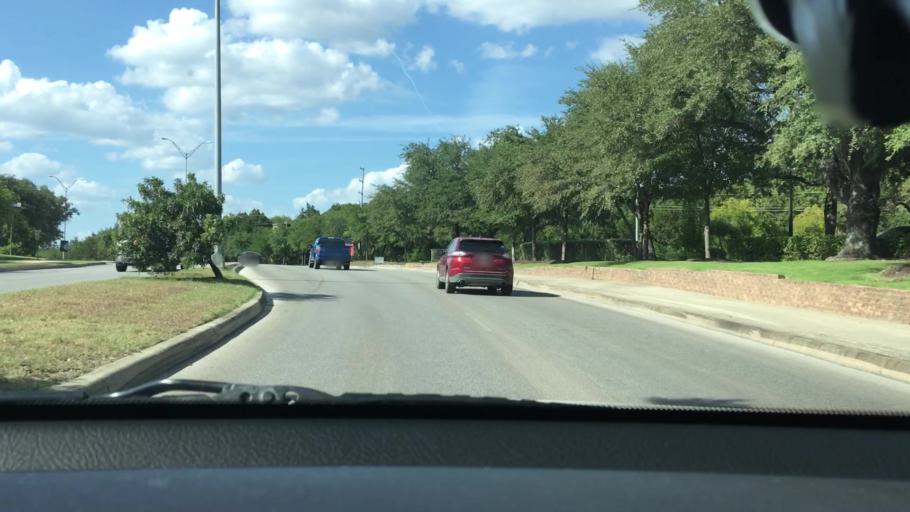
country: US
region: Texas
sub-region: Bexar County
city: Selma
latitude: 29.5902
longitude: -98.2891
